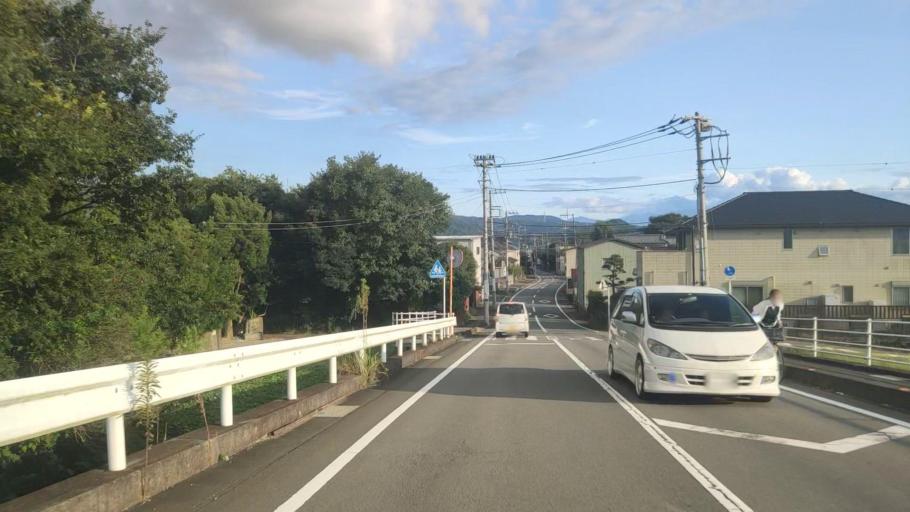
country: JP
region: Shizuoka
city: Mishima
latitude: 35.0722
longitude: 138.9500
